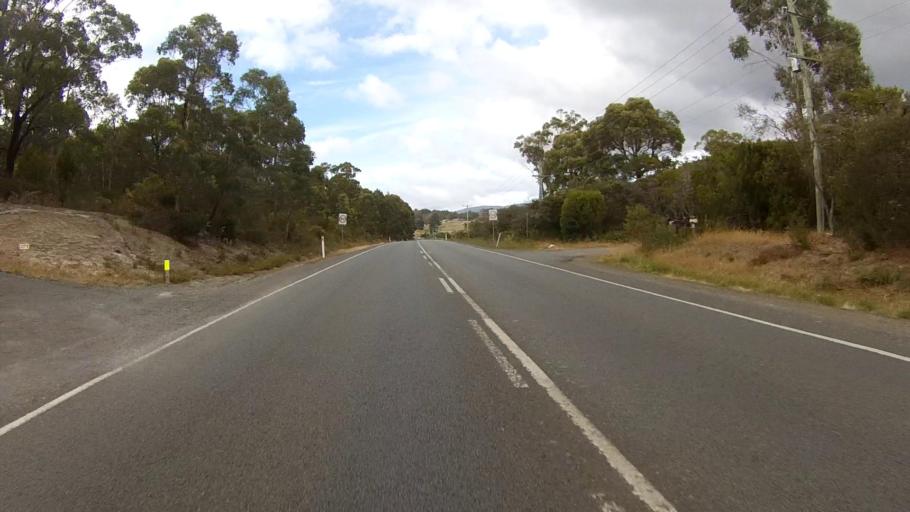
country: AU
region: Tasmania
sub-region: Kingborough
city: Kettering
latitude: -43.0794
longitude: 147.2555
